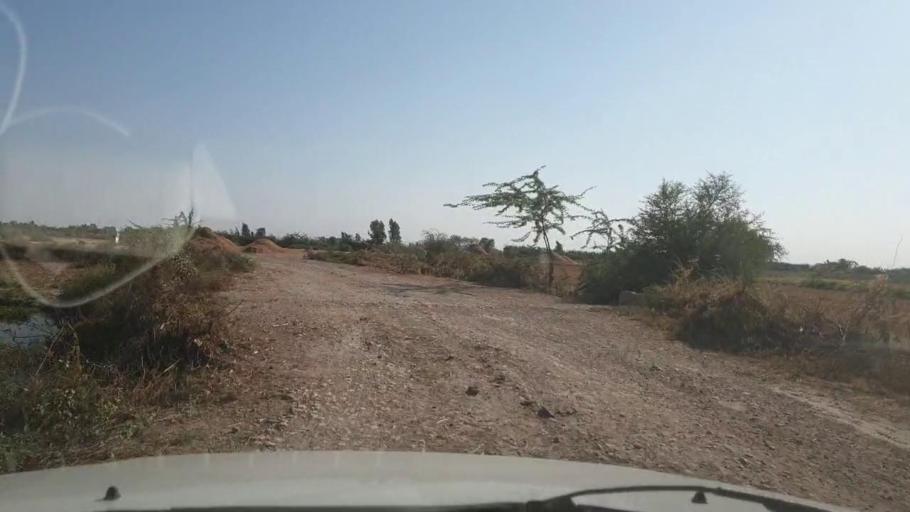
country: PK
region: Sindh
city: Mirpur Sakro
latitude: 24.4859
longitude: 67.8123
